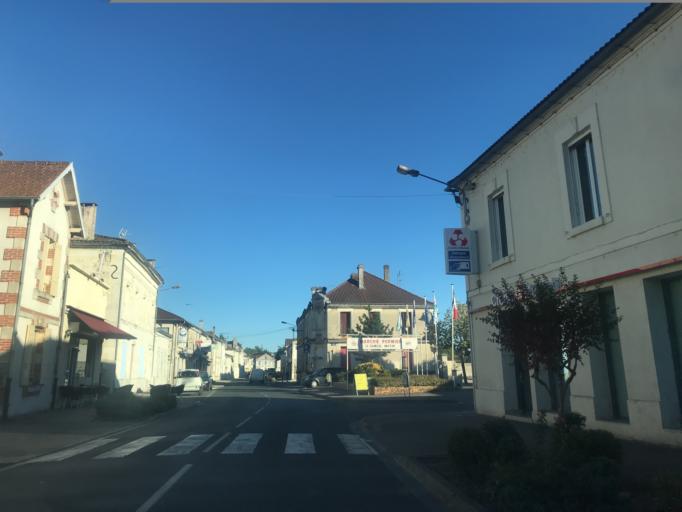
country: FR
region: Poitou-Charentes
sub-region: Departement de la Charente-Maritime
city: Saint-Aigulin
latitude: 45.1583
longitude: -0.0119
